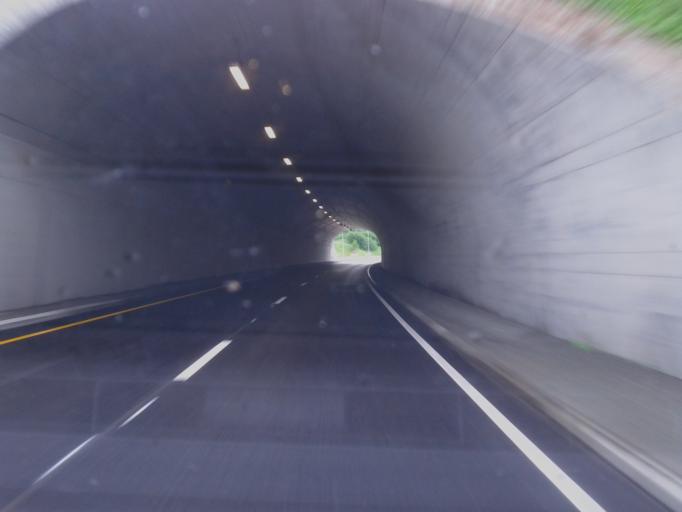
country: NO
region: Sor-Trondelag
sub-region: Melhus
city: Melhus
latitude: 63.2992
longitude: 10.2857
